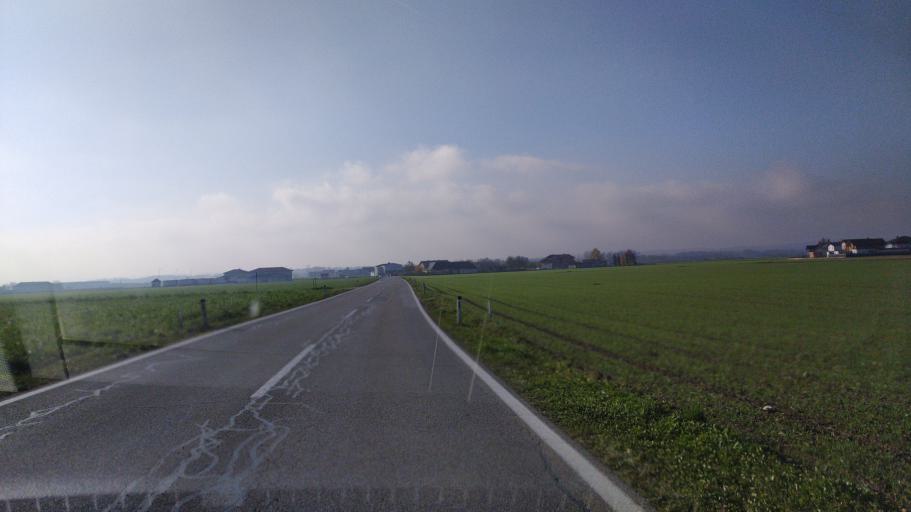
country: AT
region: Upper Austria
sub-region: Politischer Bezirk Perg
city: Perg
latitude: 48.2247
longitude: 14.6230
